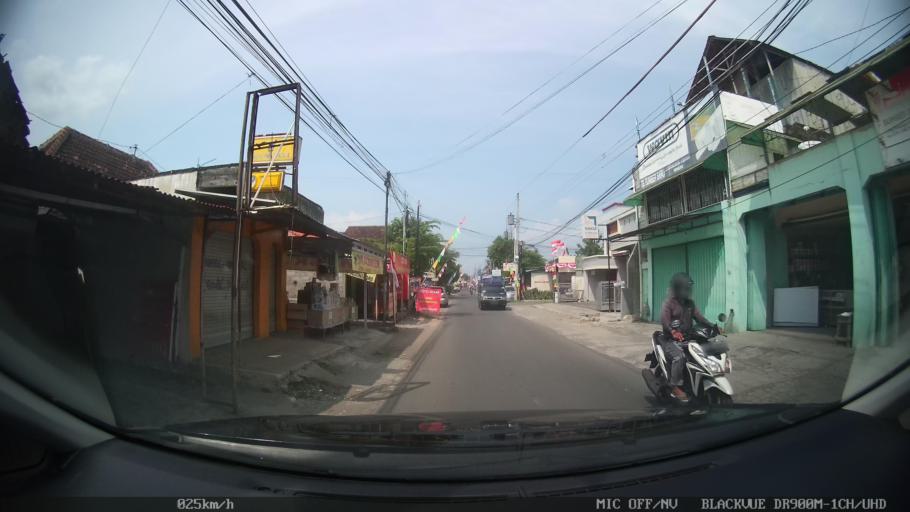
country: ID
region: Daerah Istimewa Yogyakarta
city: Depok
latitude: -7.8024
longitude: 110.4106
